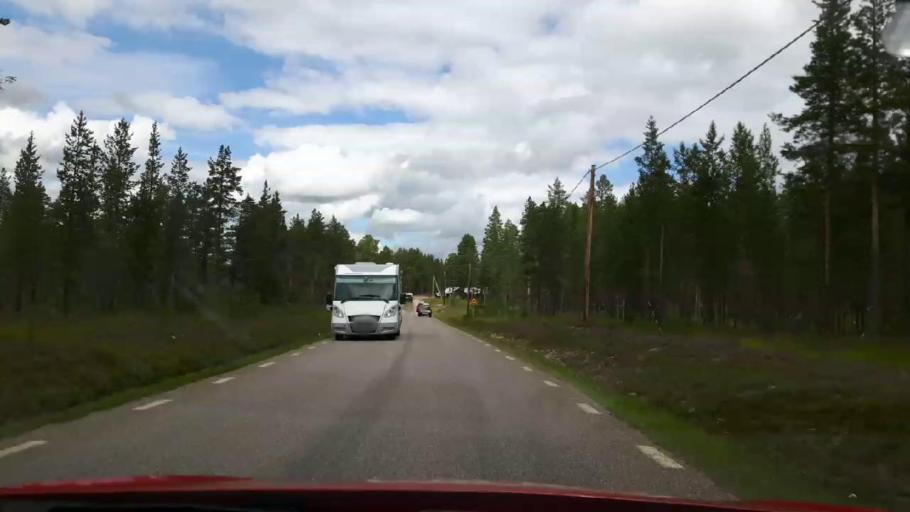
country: NO
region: Hedmark
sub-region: Trysil
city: Innbygda
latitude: 61.8299
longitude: 12.9521
